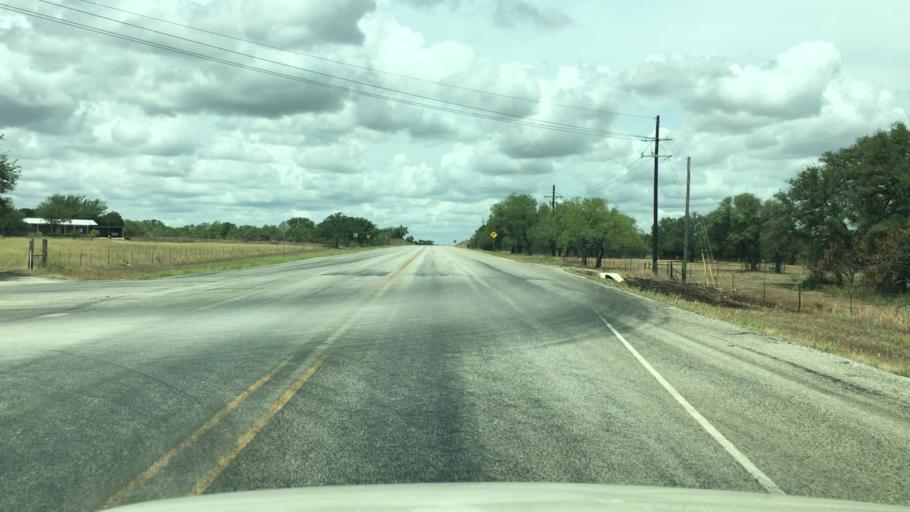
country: US
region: Texas
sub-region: McCulloch County
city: Brady
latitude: 31.0069
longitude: -99.2040
